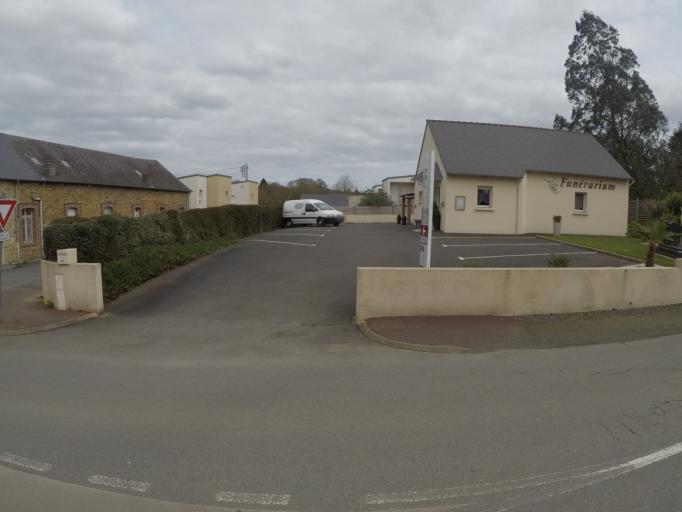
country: FR
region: Brittany
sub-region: Departement des Cotes-d'Armor
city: Plouha
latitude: 48.6717
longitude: -2.9262
